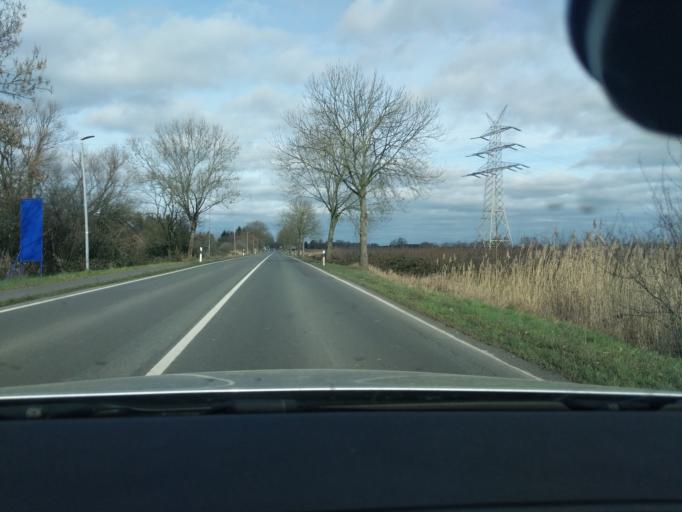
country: DE
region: Lower Saxony
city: Stade
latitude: 53.6579
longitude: 9.4760
